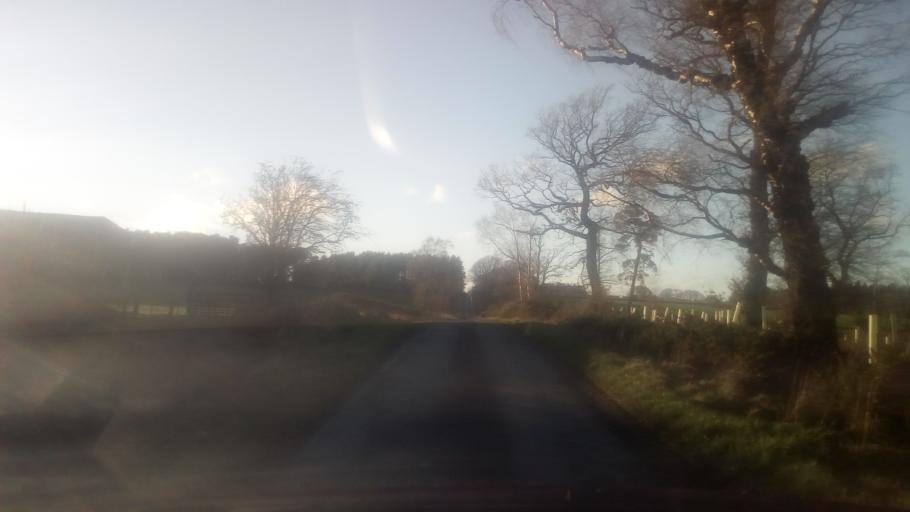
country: GB
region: Scotland
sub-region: The Scottish Borders
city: Jedburgh
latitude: 55.4709
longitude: -2.4451
